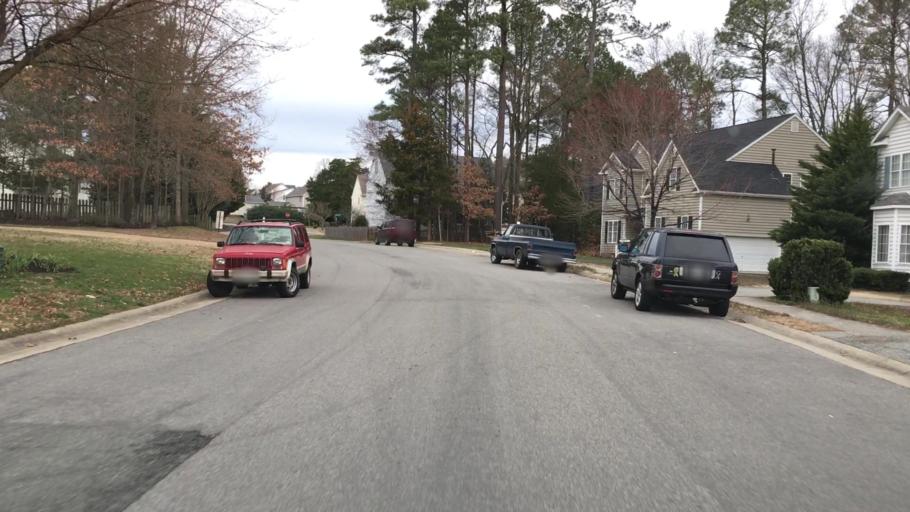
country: US
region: Virginia
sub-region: Henrico County
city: Short Pump
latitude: 37.6513
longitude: -77.5694
